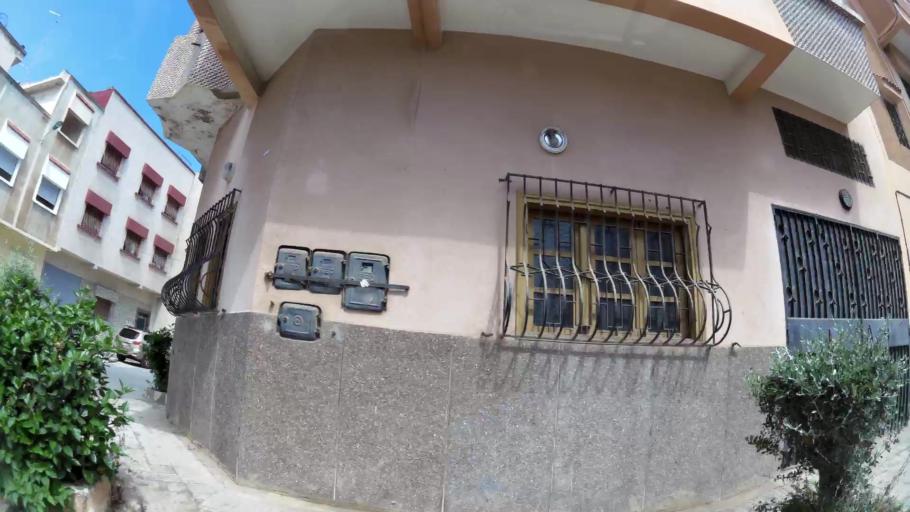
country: MA
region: Rabat-Sale-Zemmour-Zaer
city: Sale
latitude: 34.0696
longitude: -6.7914
